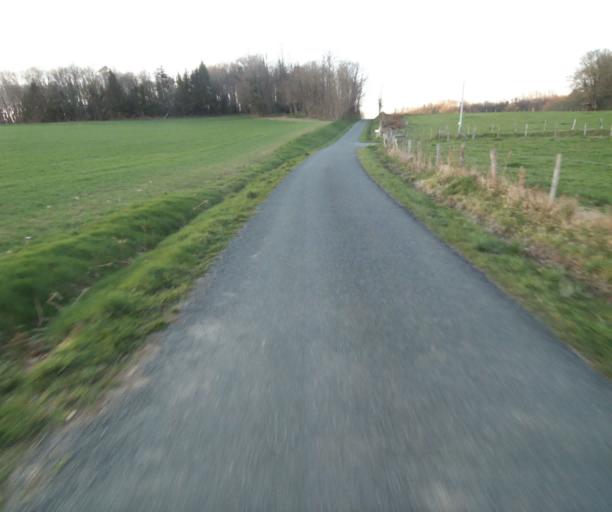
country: FR
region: Limousin
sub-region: Departement de la Correze
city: Uzerche
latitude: 45.3795
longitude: 1.6033
